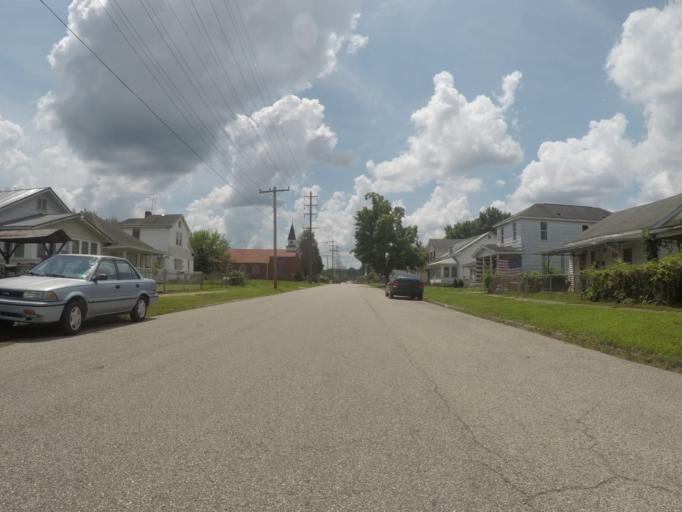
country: US
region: West Virginia
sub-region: Cabell County
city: Huntington
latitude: 38.4251
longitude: -82.3869
